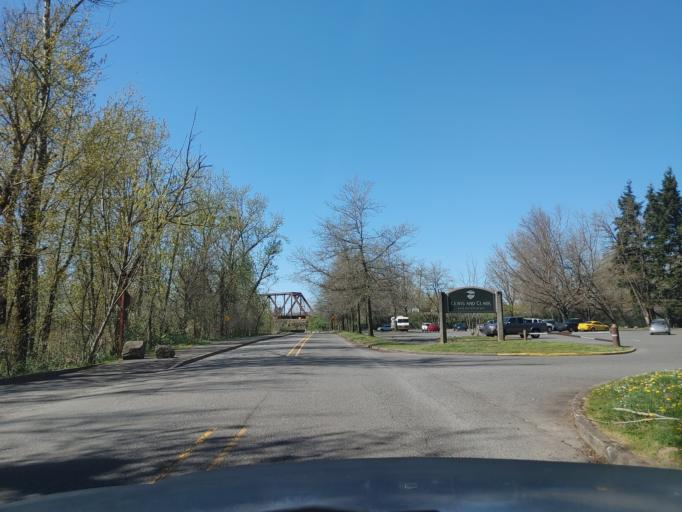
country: US
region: Oregon
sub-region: Multnomah County
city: Troutdale
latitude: 45.5409
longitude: -122.3796
